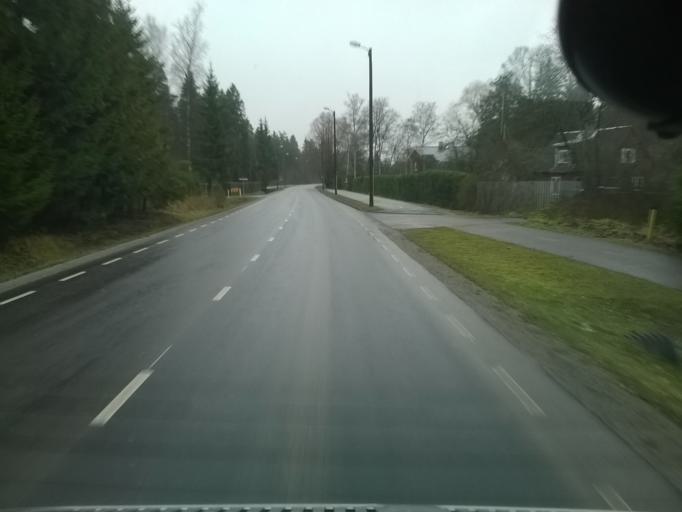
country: EE
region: Harju
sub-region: Saku vald
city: Saku
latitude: 59.2225
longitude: 24.6720
